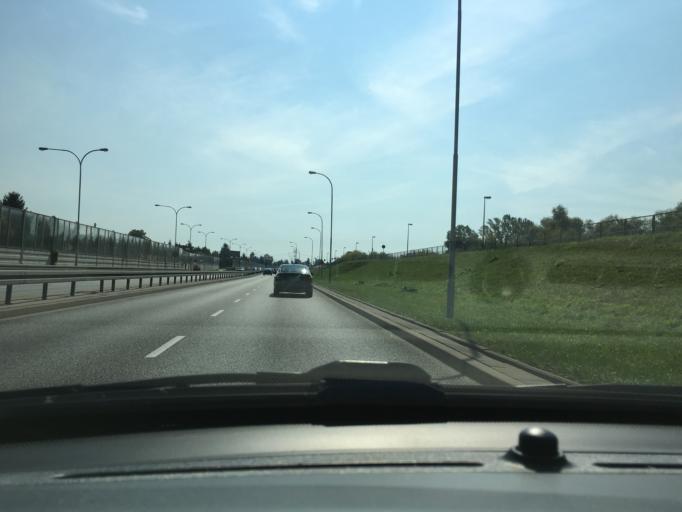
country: PL
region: Masovian Voivodeship
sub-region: Warszawa
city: Praga Poludnie
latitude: 52.2091
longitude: 21.1081
